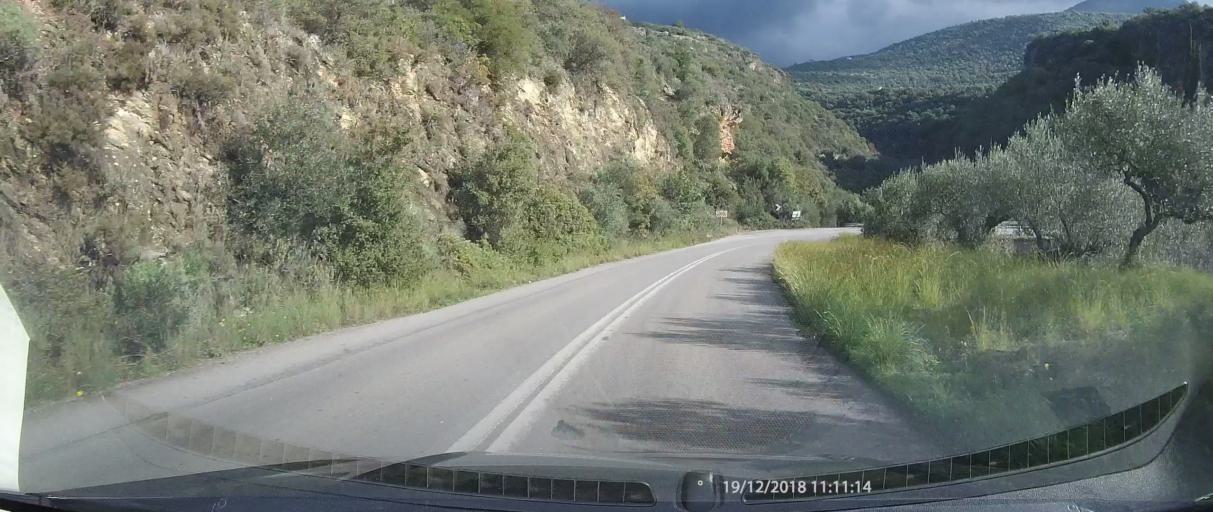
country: GR
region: Peloponnese
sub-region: Nomos Messinias
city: Kardamyli
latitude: 36.8208
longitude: 22.3023
